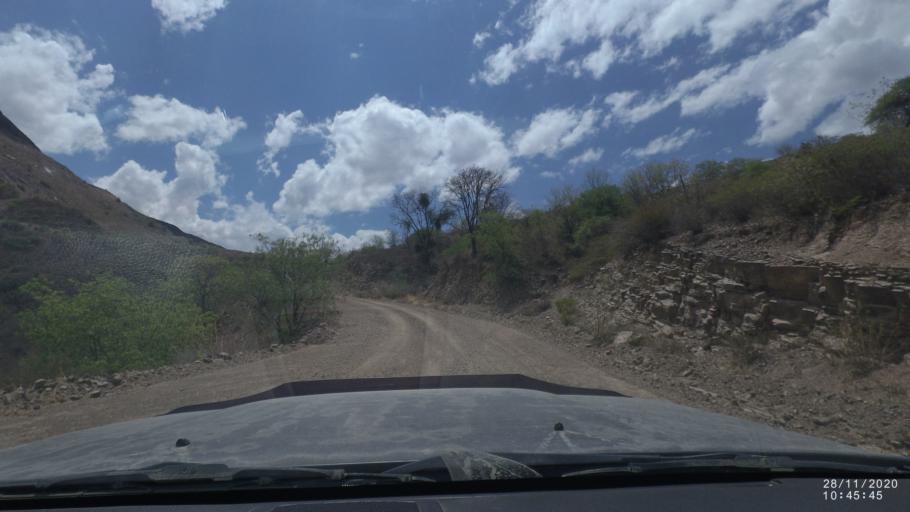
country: BO
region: Cochabamba
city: Capinota
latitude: -17.7868
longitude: -66.1291
